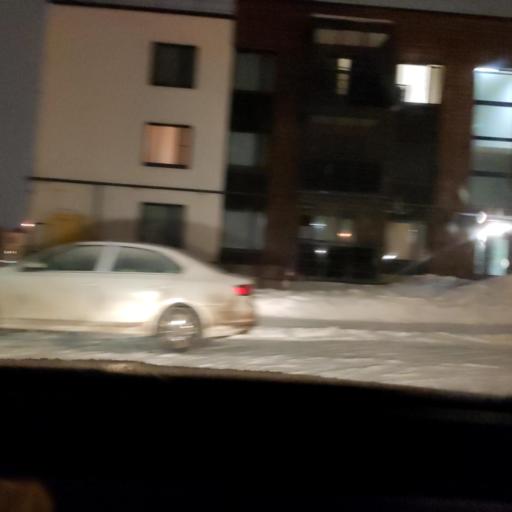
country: RU
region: Moskovskaya
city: Rozhdestveno
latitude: 55.8043
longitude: 36.9884
